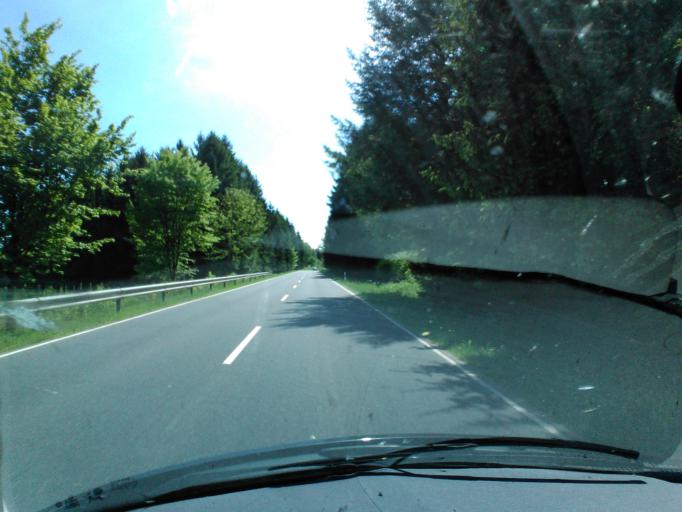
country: DE
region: Rheinland-Pfalz
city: Winterspelt
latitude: 50.2076
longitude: 6.2283
